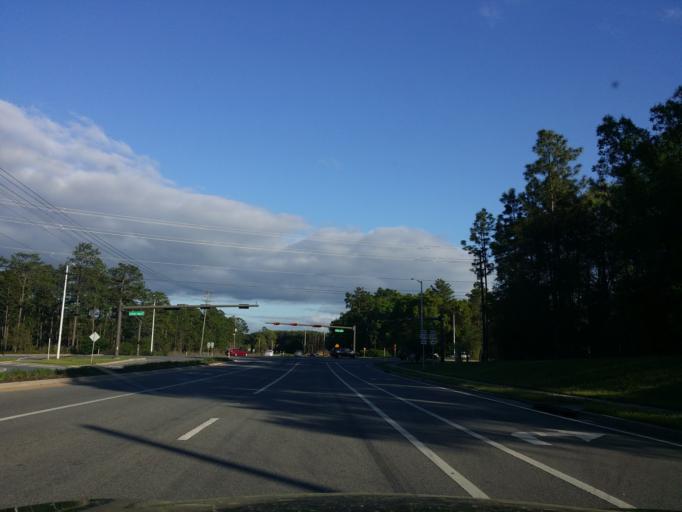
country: US
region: Florida
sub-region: Leon County
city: Woodville
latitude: 30.3817
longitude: -84.2377
